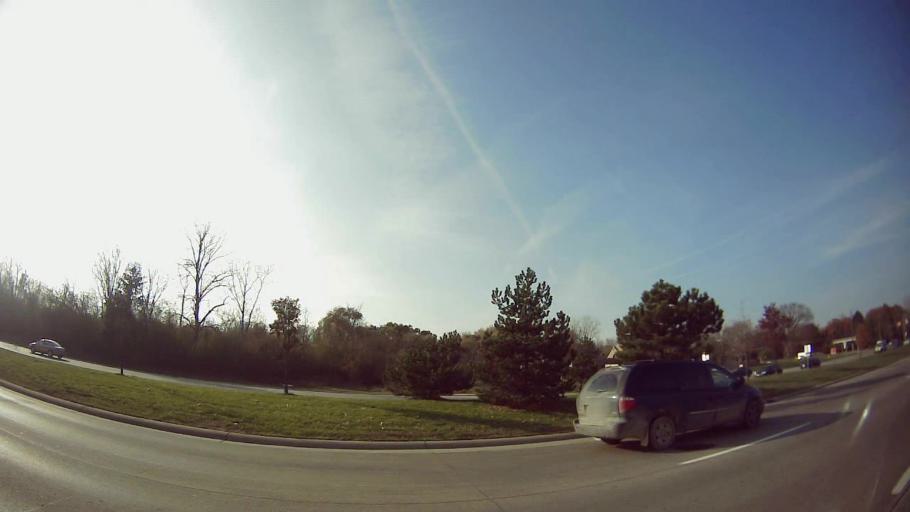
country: US
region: Michigan
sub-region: Oakland County
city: Bingham Farms
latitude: 42.5143
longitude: -83.2855
